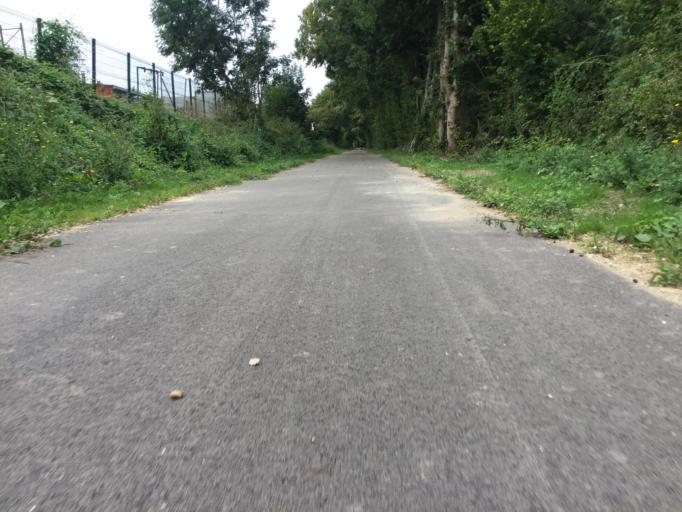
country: FR
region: Picardie
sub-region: Departement de l'Oise
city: Saint-Paul
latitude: 49.3998
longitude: 2.0125
